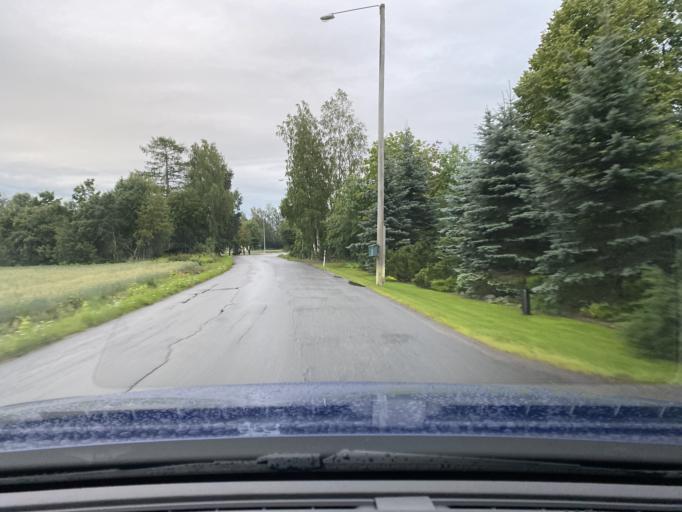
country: FI
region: Ostrobothnia
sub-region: Kyroenmaa
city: Laihia
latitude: 62.9831
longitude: 21.9977
